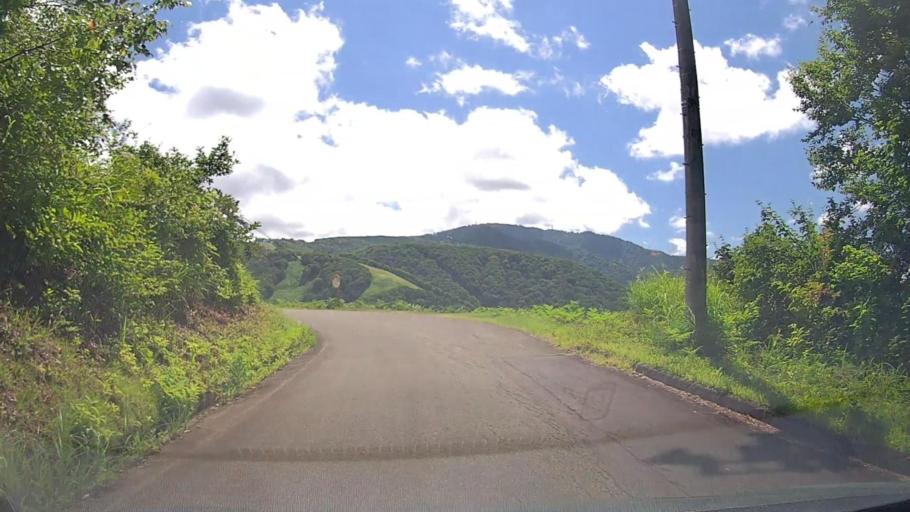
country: JP
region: Nagano
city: Iiyama
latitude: 36.9344
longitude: 138.4558
